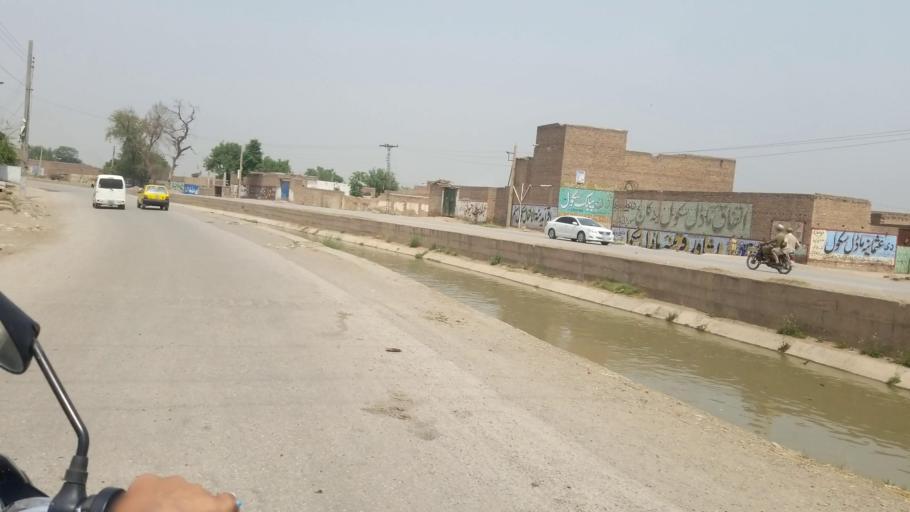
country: PK
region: Khyber Pakhtunkhwa
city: Peshawar
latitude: 33.9564
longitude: 71.5501
